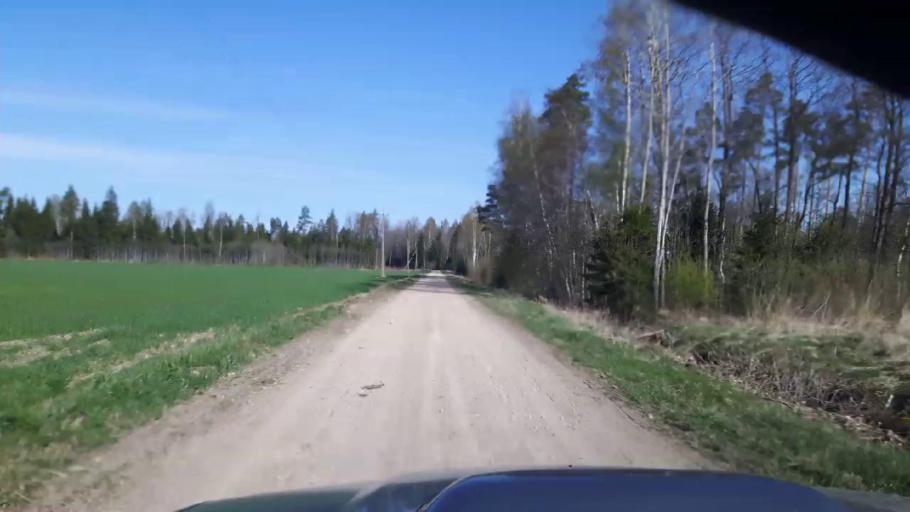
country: EE
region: Paernumaa
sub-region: Tootsi vald
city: Tootsi
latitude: 58.5143
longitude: 24.9287
